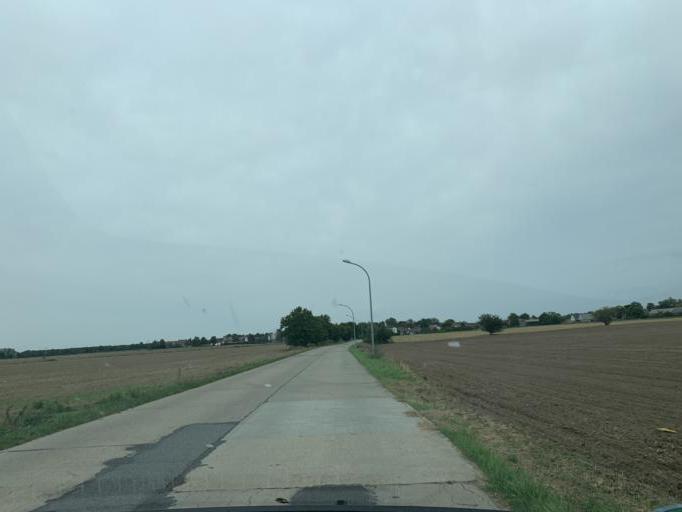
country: DE
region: Brandenburg
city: Zehdenick
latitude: 53.0092
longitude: 13.2766
